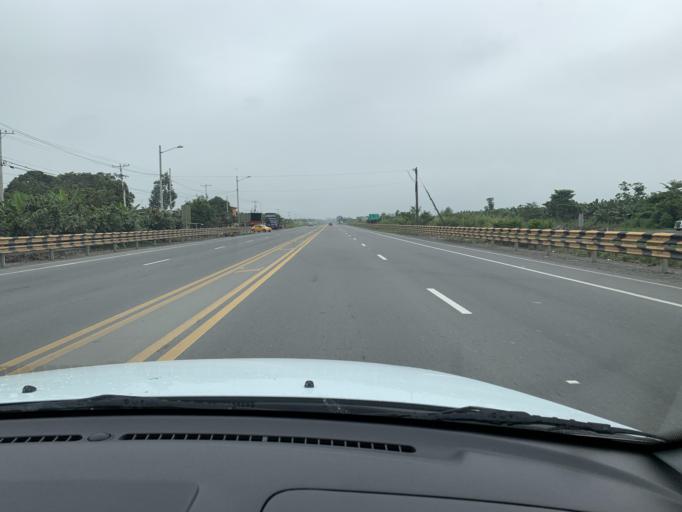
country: EC
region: Guayas
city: Coronel Marcelino Mariduena
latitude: -2.2935
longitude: -79.5010
